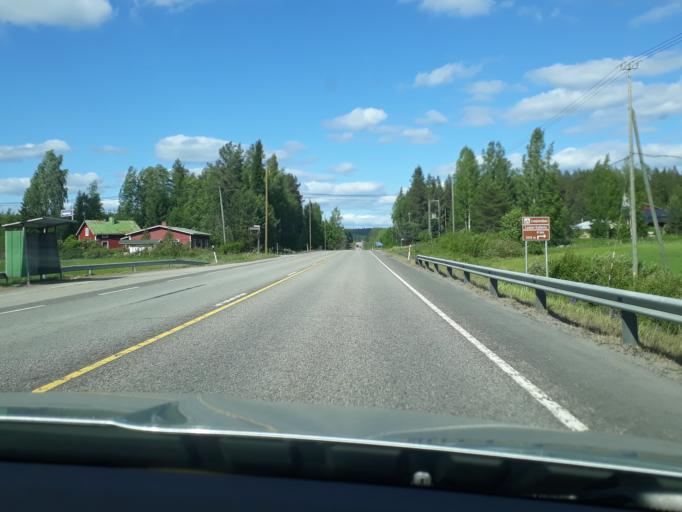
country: FI
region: Central Finland
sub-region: AEaenekoski
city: AEaenekoski
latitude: 62.6546
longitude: 25.7233
